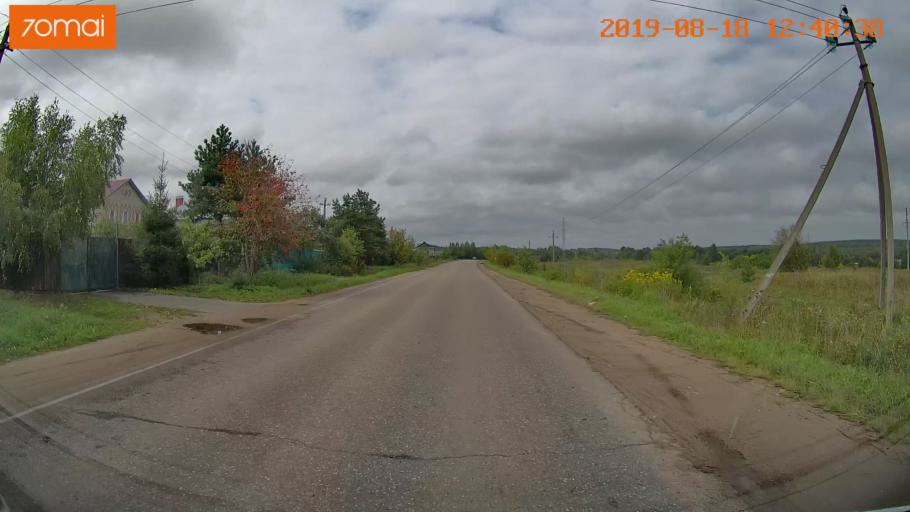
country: RU
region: Ivanovo
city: Novo-Talitsy
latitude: 57.0325
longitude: 40.9033
